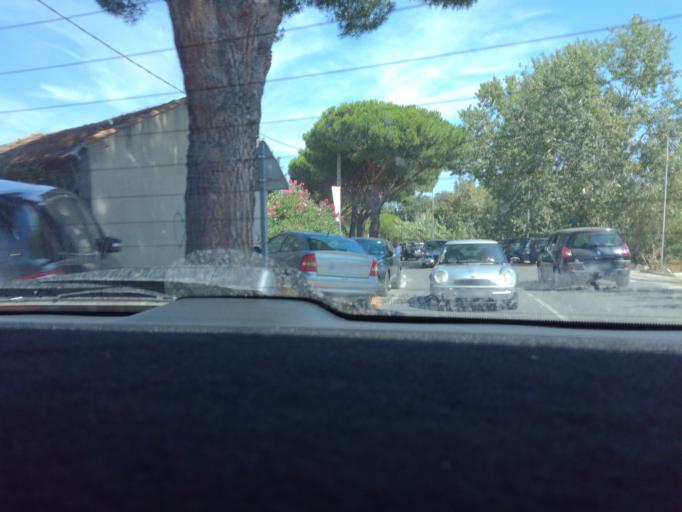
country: FR
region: Provence-Alpes-Cote d'Azur
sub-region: Departement du Var
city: Hyeres
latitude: 43.0374
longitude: 6.1445
